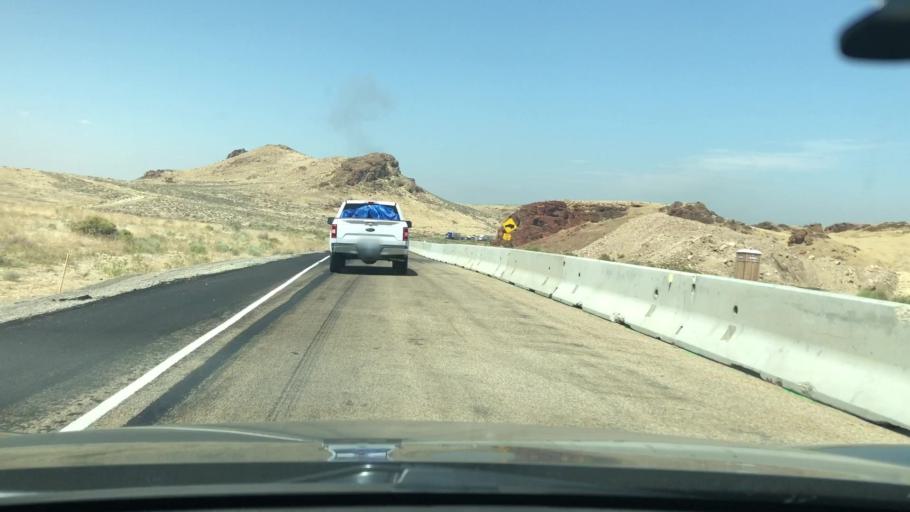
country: US
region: Idaho
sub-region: Owyhee County
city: Marsing
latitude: 43.4572
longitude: -116.8640
